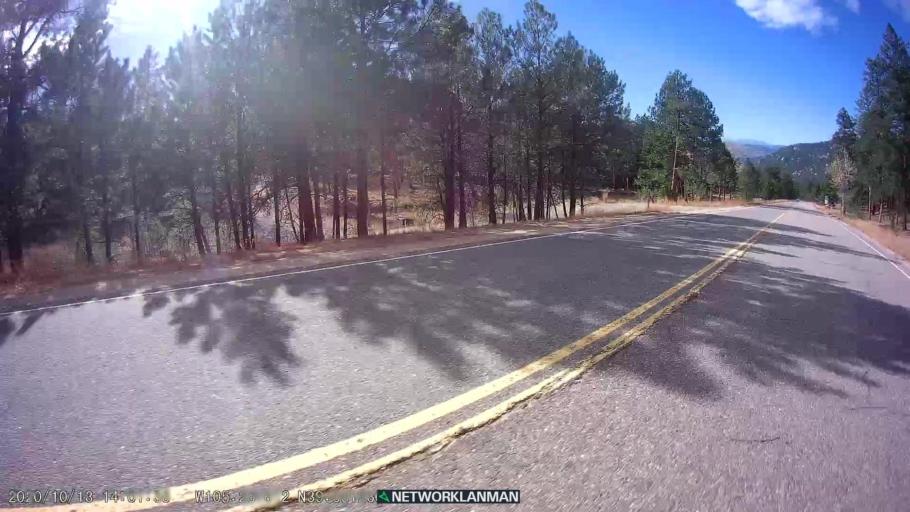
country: US
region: Colorado
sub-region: Douglas County
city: Roxborough Park
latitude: 39.3814
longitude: -105.2615
